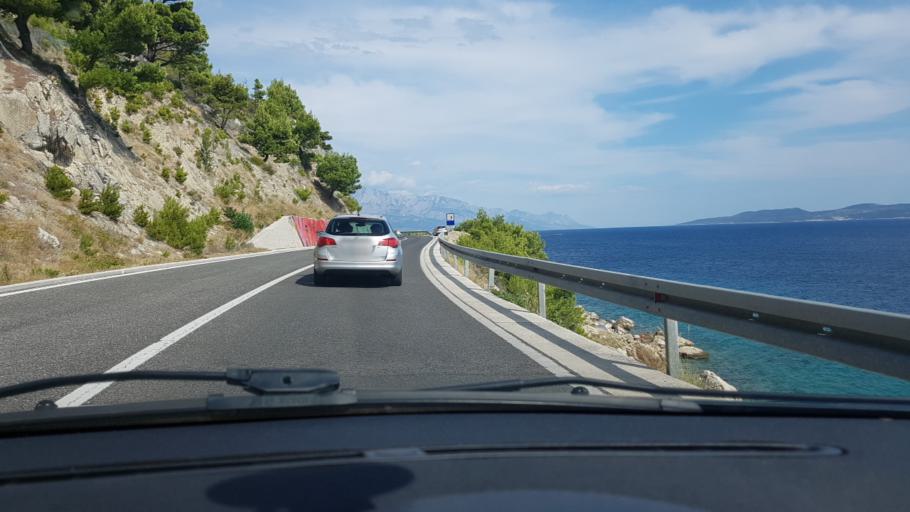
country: HR
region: Splitsko-Dalmatinska
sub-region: Grad Omis
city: Omis
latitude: 43.4093
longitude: 16.7644
